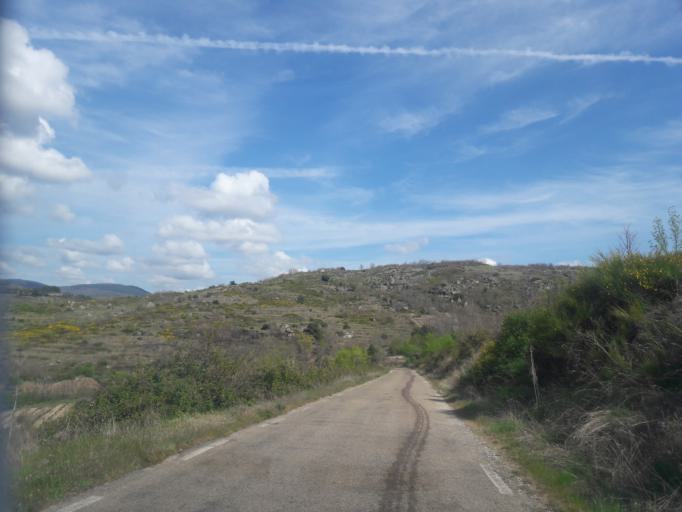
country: ES
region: Castille and Leon
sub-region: Provincia de Salamanca
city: San Esteban de la Sierra
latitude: 40.5072
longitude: -5.8859
